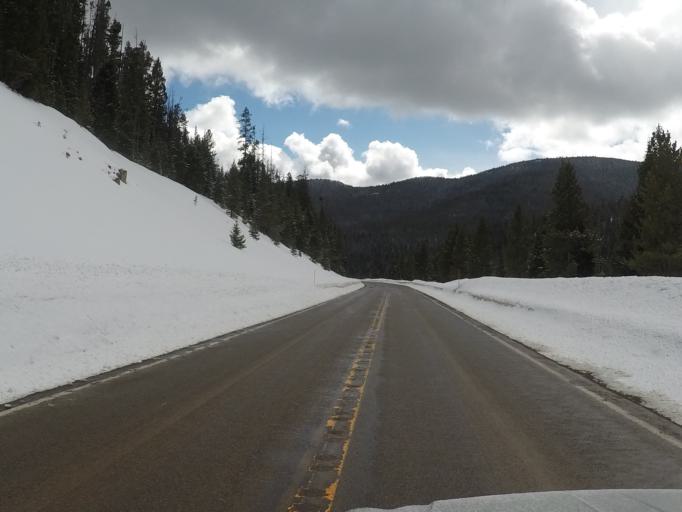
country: US
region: Montana
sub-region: Meagher County
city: White Sulphur Springs
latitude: 46.8144
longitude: -110.7039
